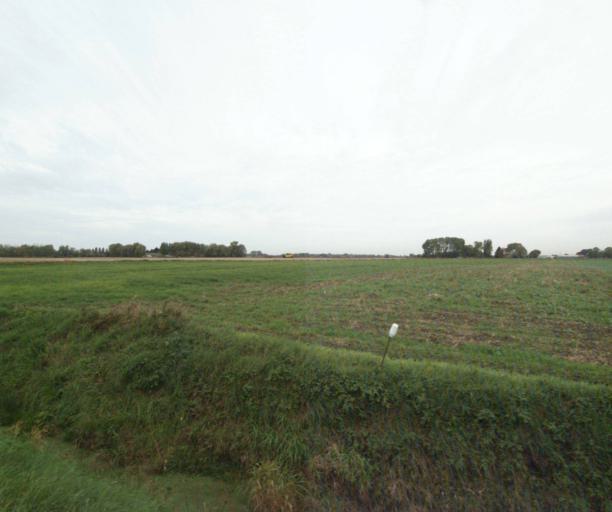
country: FR
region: Nord-Pas-de-Calais
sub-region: Departement du Pas-de-Calais
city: Lorgies
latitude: 50.5909
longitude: 2.7977
